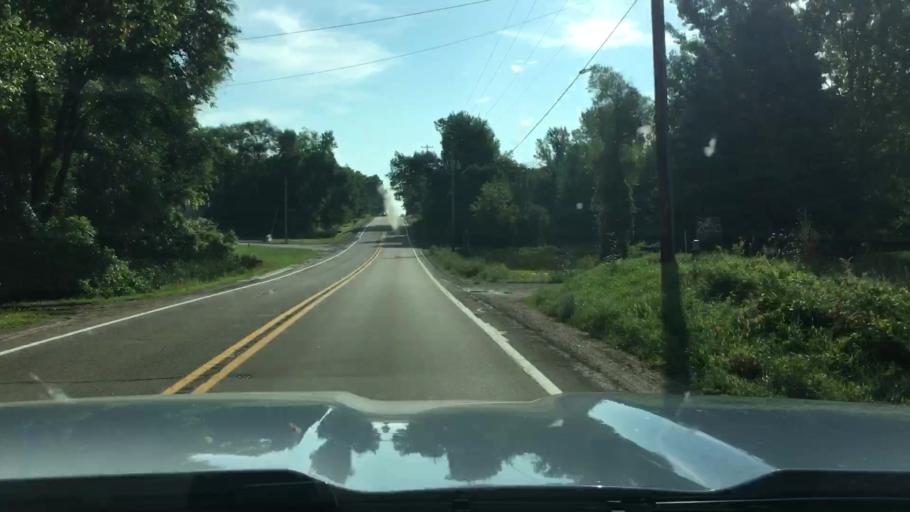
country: US
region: Michigan
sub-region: Kent County
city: Cedar Springs
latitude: 43.2195
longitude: -85.6207
